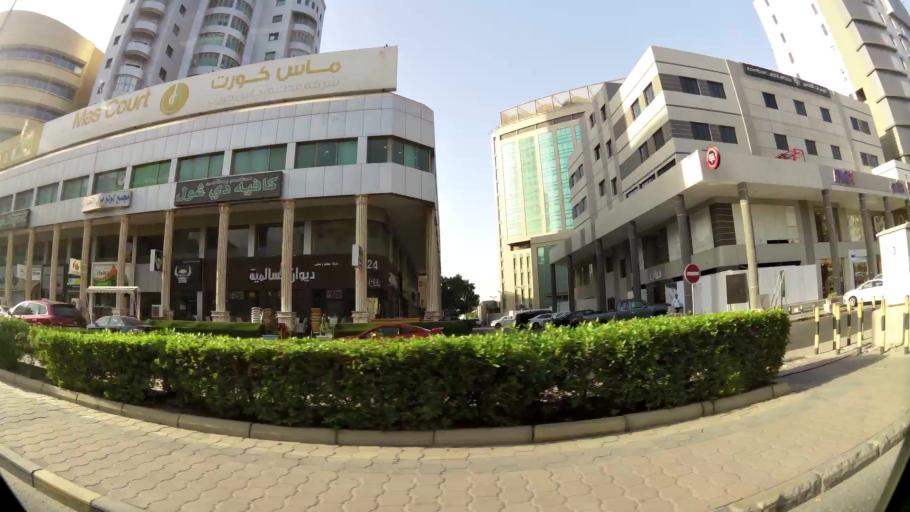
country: KW
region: Muhafazat Hawalli
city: As Salimiyah
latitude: 29.3469
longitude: 48.0882
